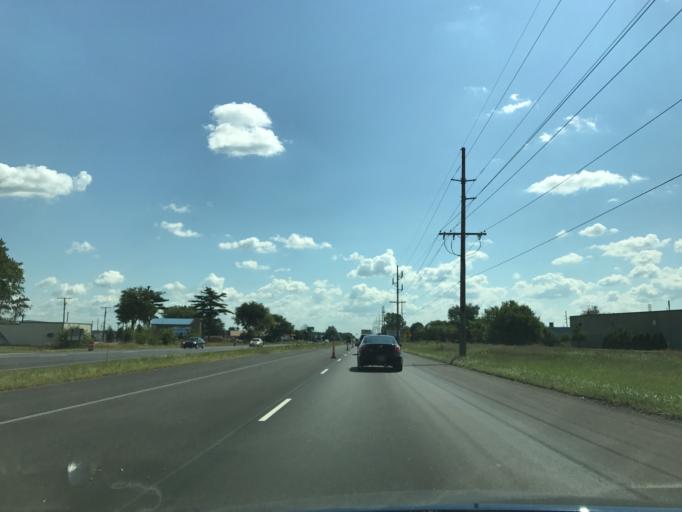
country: US
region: Indiana
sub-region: Porter County
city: Valparaiso
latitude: 41.4487
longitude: -87.0160
